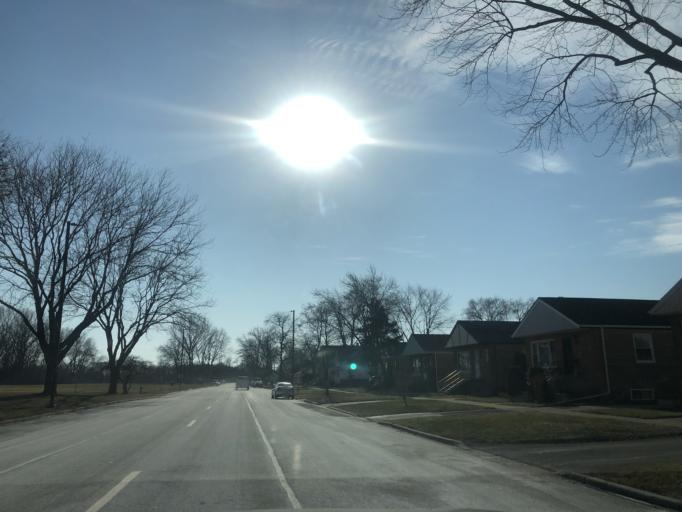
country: US
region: Illinois
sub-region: Cook County
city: Stickney
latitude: 41.8170
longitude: -87.7827
